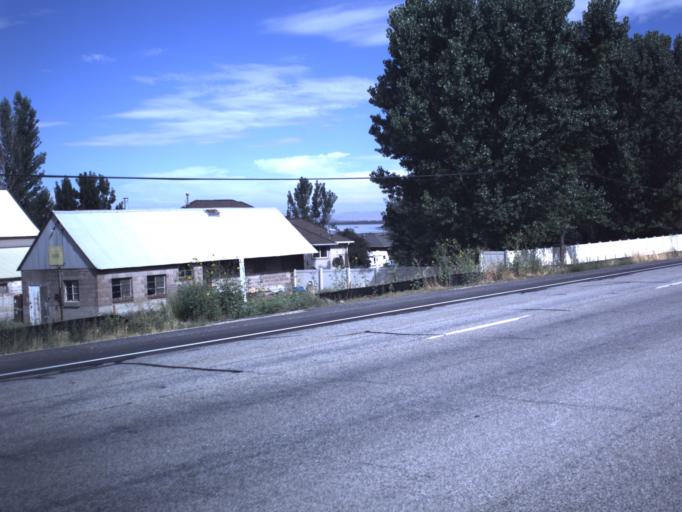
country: US
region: Utah
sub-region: Box Elder County
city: South Willard
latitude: 41.3754
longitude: -112.0332
